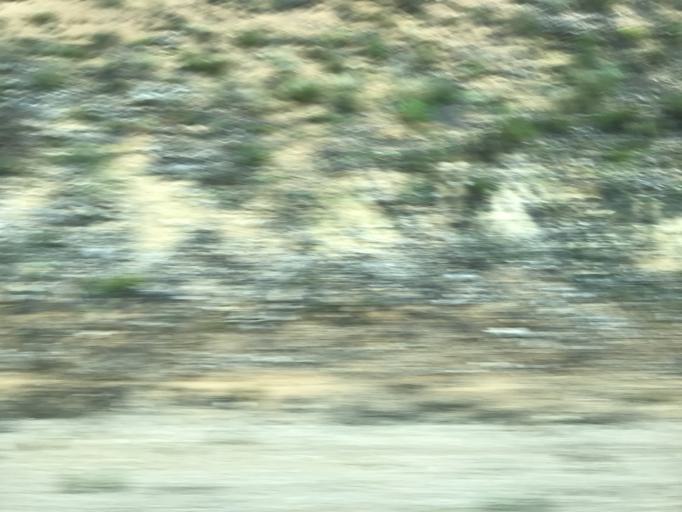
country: ES
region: Castille and Leon
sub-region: Provincia de Burgos
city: Quintanilla de la Mata
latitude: 41.9691
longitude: -3.7778
